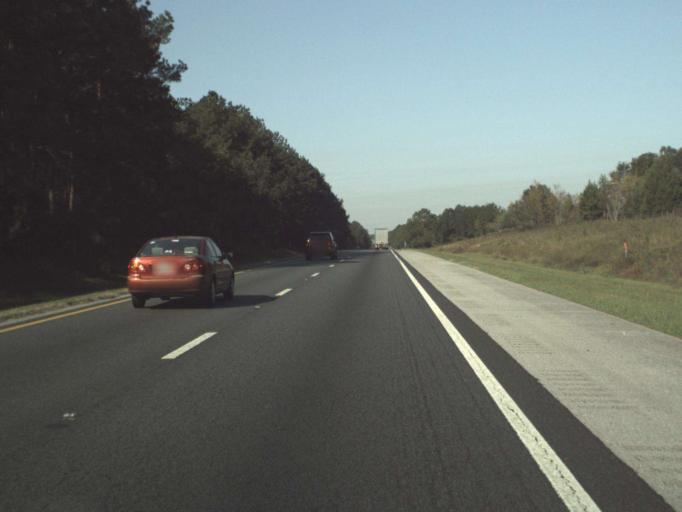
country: US
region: Florida
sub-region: Holmes County
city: Bonifay
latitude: 30.7611
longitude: -85.7560
